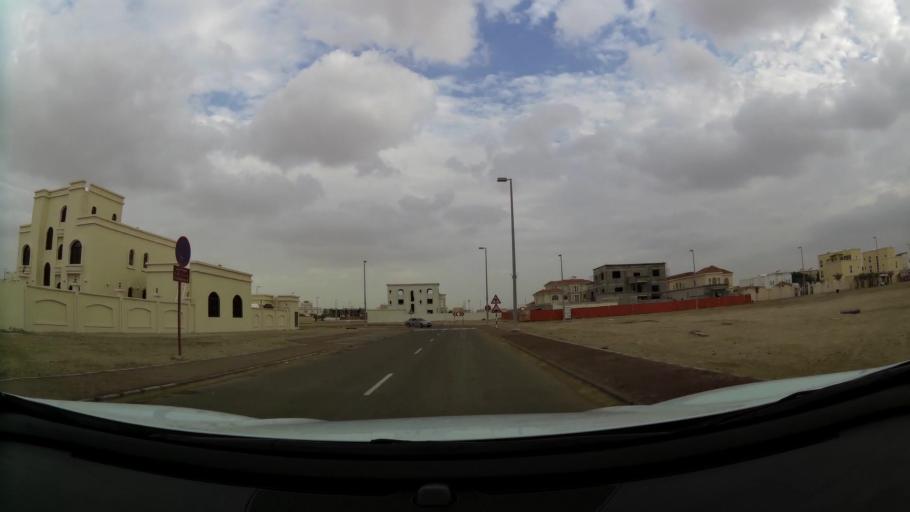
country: AE
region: Abu Dhabi
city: Abu Dhabi
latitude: 24.3487
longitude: 54.6182
